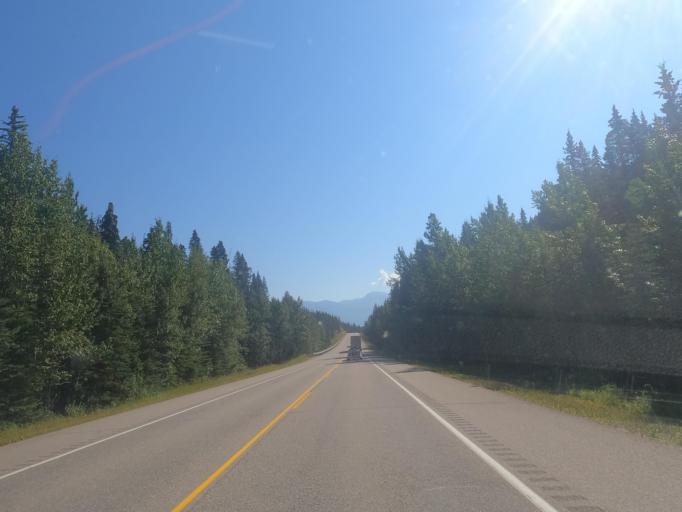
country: CA
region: Alberta
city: Jasper Park Lodge
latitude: 52.8608
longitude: -118.1892
